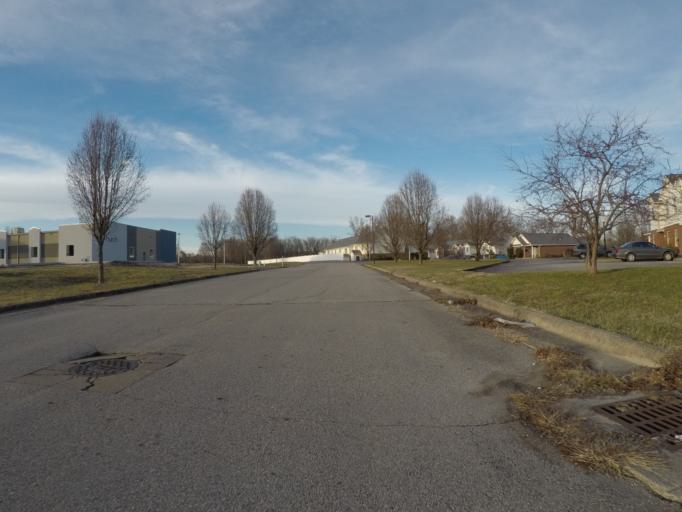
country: US
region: Ohio
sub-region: Lawrence County
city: Burlington
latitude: 38.4020
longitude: -82.4905
